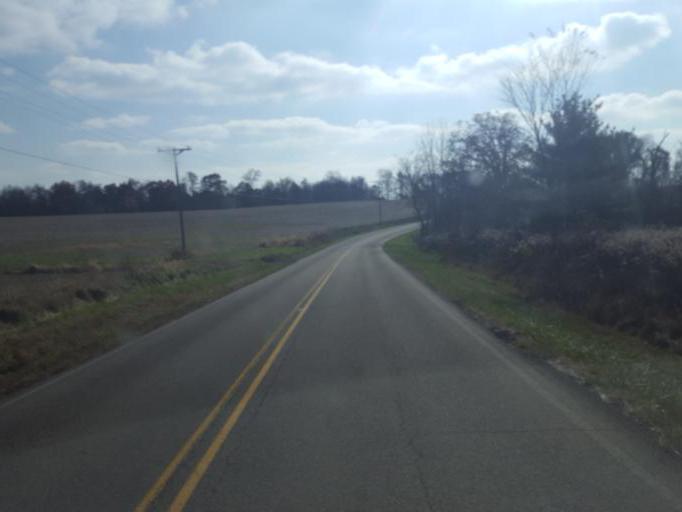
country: US
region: Ohio
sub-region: Knox County
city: Oak Hill
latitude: 40.4514
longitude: -82.1291
